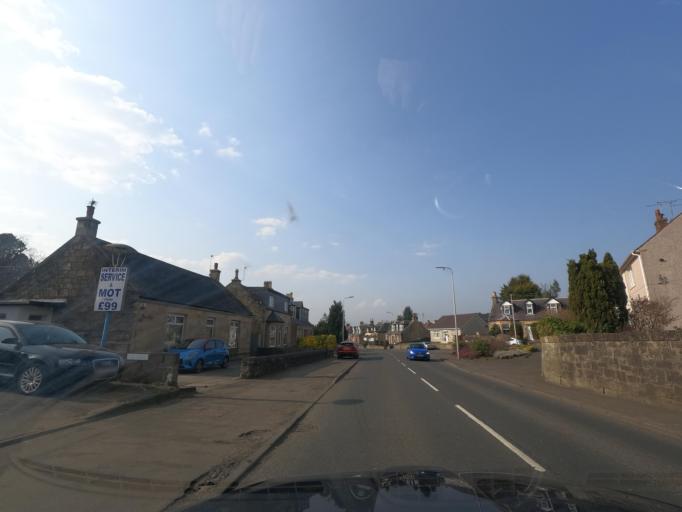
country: GB
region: Scotland
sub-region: Falkirk
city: Grangemouth
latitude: 55.9875
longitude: -3.7397
